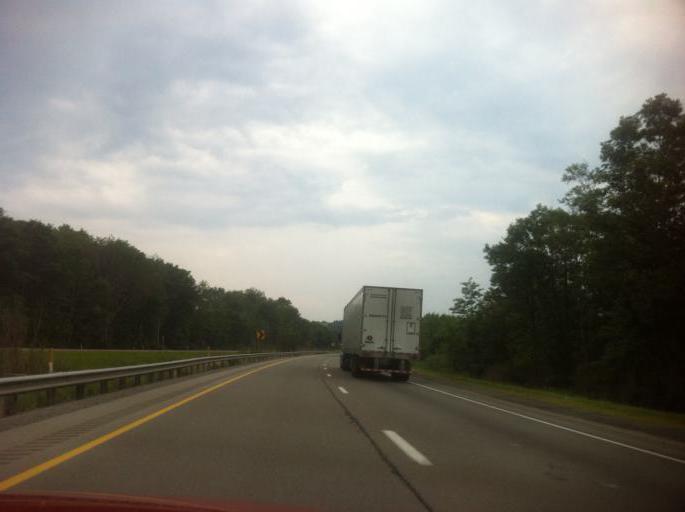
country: US
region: Pennsylvania
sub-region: Jefferson County
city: Brookville
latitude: 41.1854
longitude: -79.1904
